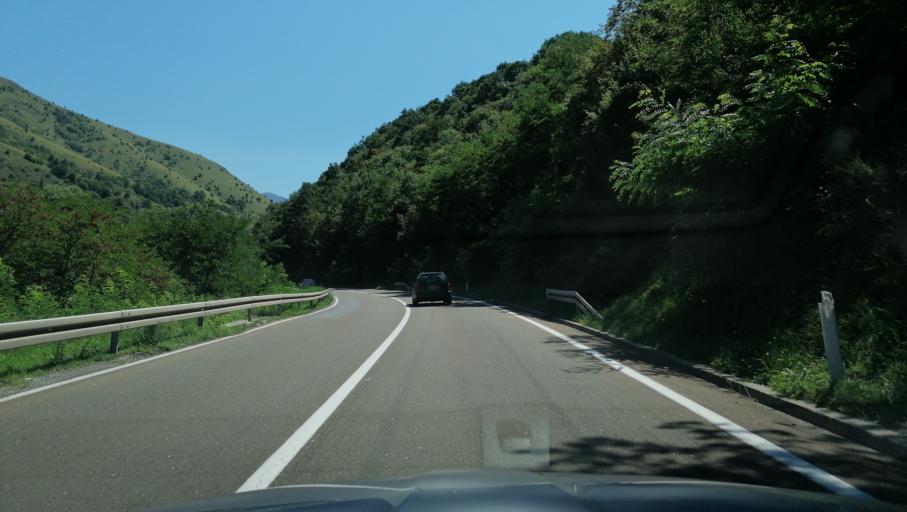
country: RS
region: Central Serbia
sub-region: Raski Okrug
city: Kraljevo
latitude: 43.5762
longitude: 20.5879
